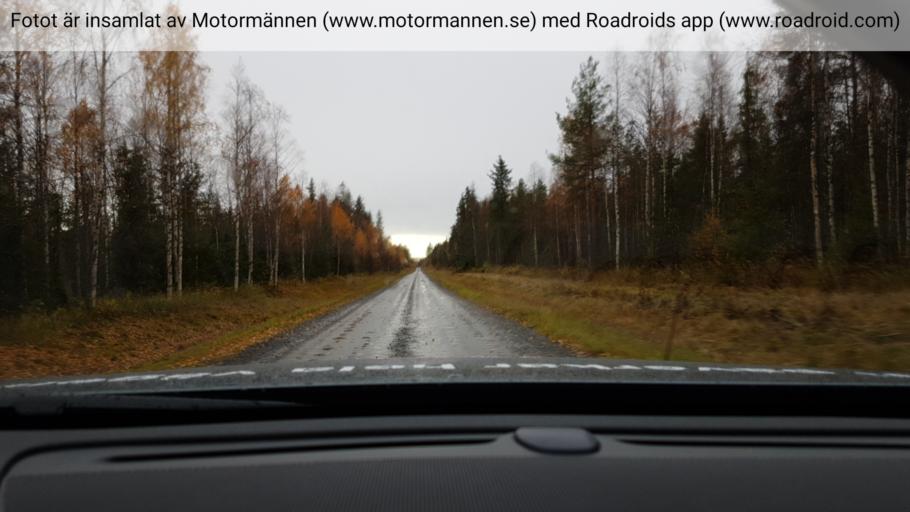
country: SE
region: Norrbotten
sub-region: Pajala Kommun
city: Pajala
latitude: 66.9758
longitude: 22.9024
